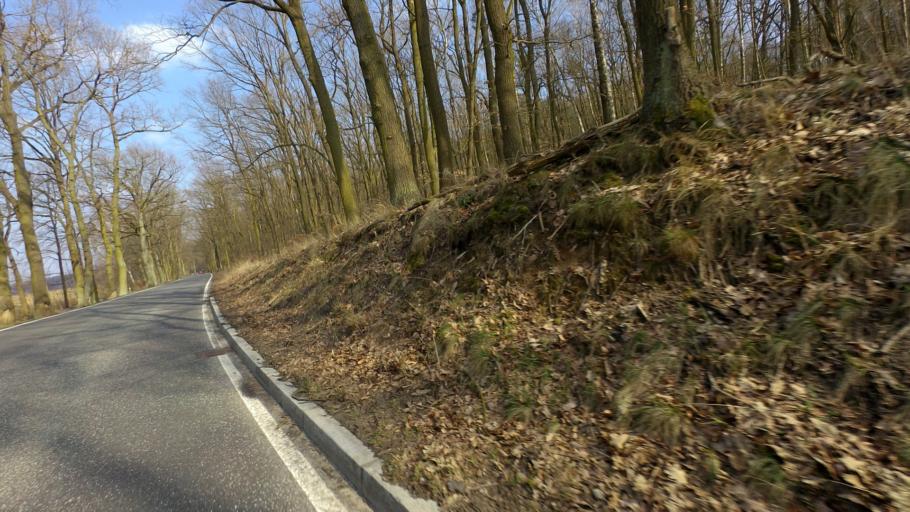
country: DE
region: Brandenburg
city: Werder
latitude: 52.3235
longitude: 12.9567
